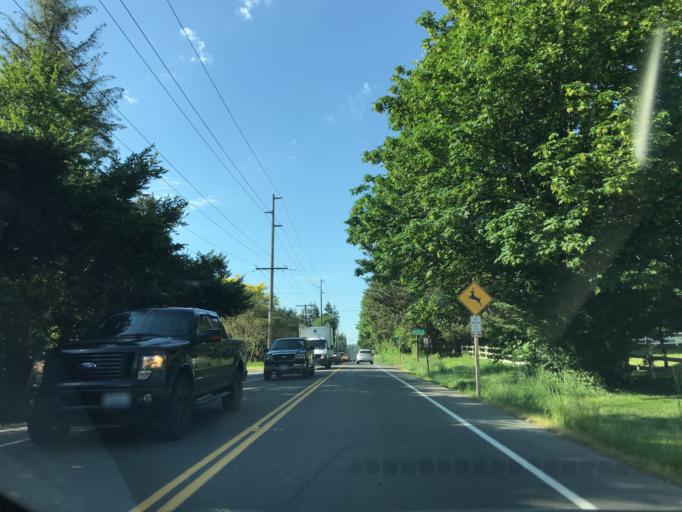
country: US
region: Washington
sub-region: King County
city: Issaquah
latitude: 47.5024
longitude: -122.0224
